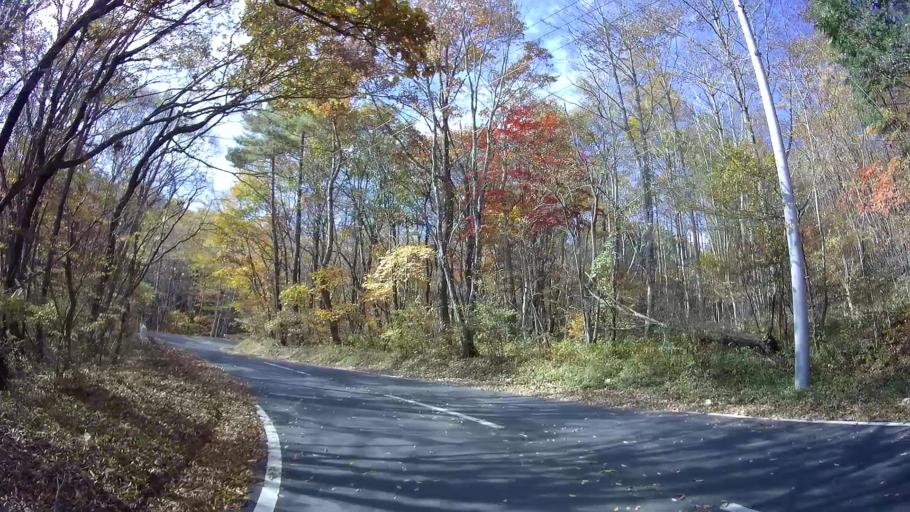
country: JP
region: Gunma
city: Nakanojomachi
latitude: 36.5194
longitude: 138.6640
